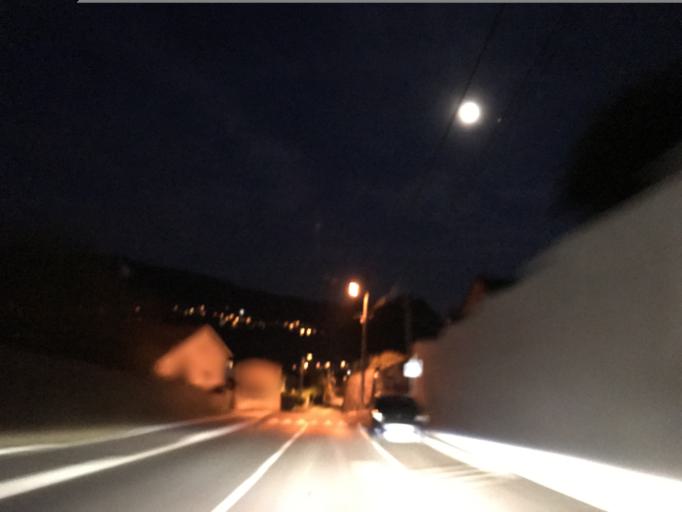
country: FR
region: Auvergne
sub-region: Departement du Puy-de-Dome
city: Thiers
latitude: 45.8579
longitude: 3.5343
